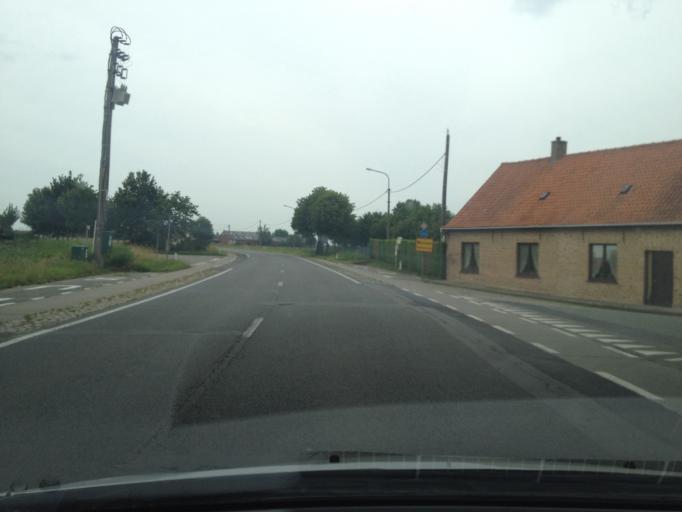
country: BE
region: Flanders
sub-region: Provincie West-Vlaanderen
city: Diksmuide
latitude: 50.9860
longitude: 2.8738
